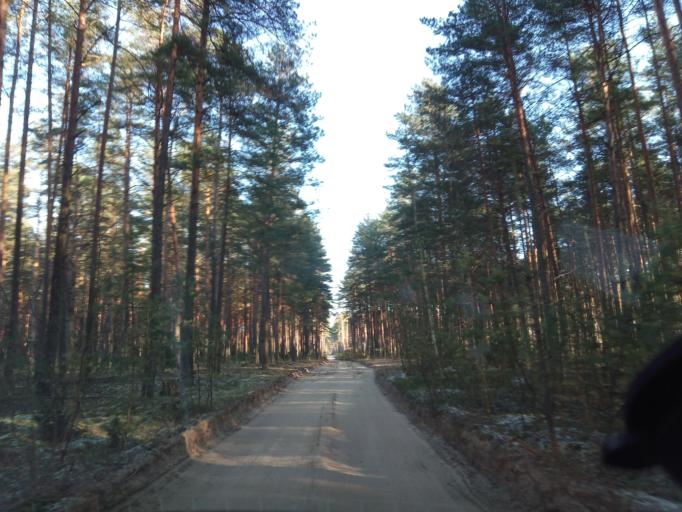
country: LT
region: Alytaus apskritis
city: Druskininkai
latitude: 53.9567
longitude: 23.8723
